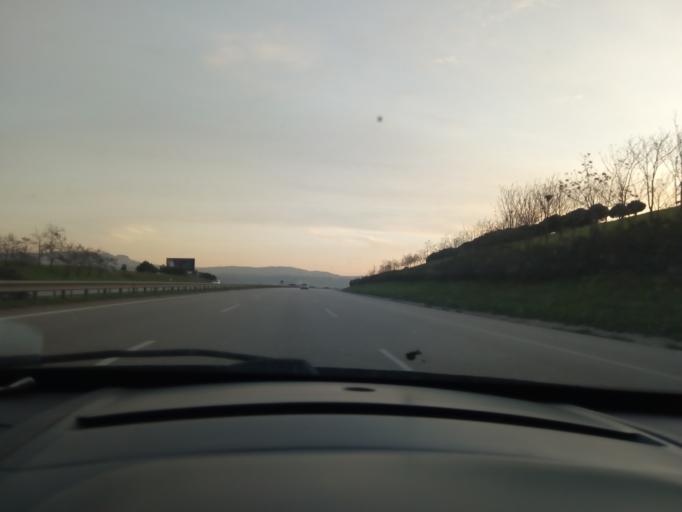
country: TR
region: Bursa
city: Niluefer
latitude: 40.2701
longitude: 28.9596
